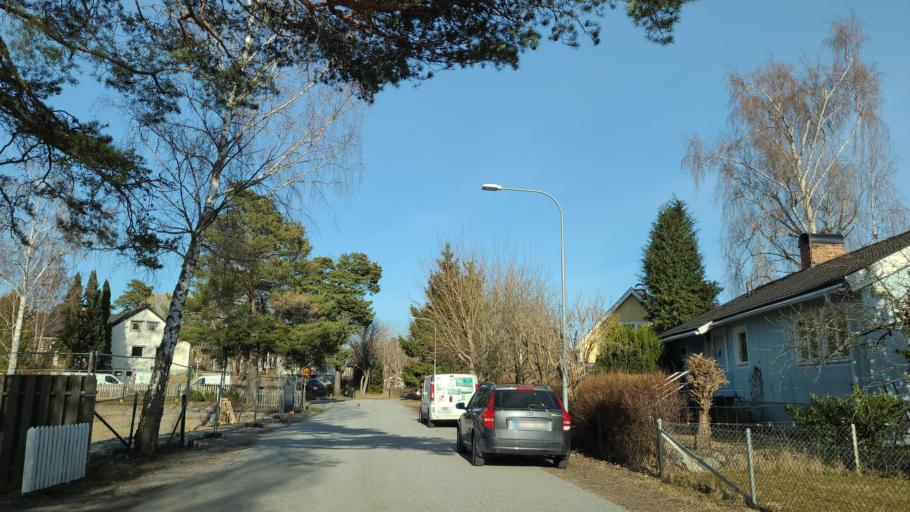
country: SE
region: Stockholm
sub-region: Ekero Kommun
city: Ekeroe
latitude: 59.2739
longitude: 17.7855
